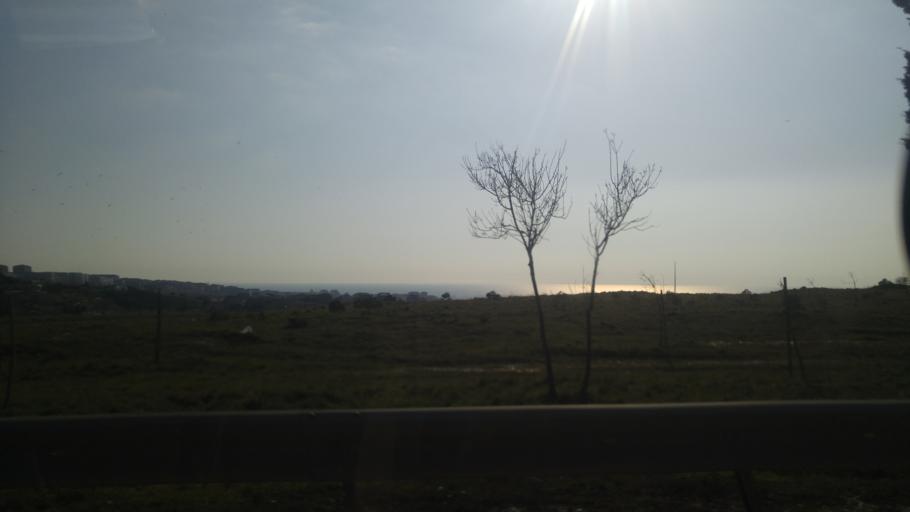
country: TR
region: Istanbul
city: Gurpinar
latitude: 41.0247
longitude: 28.6216
